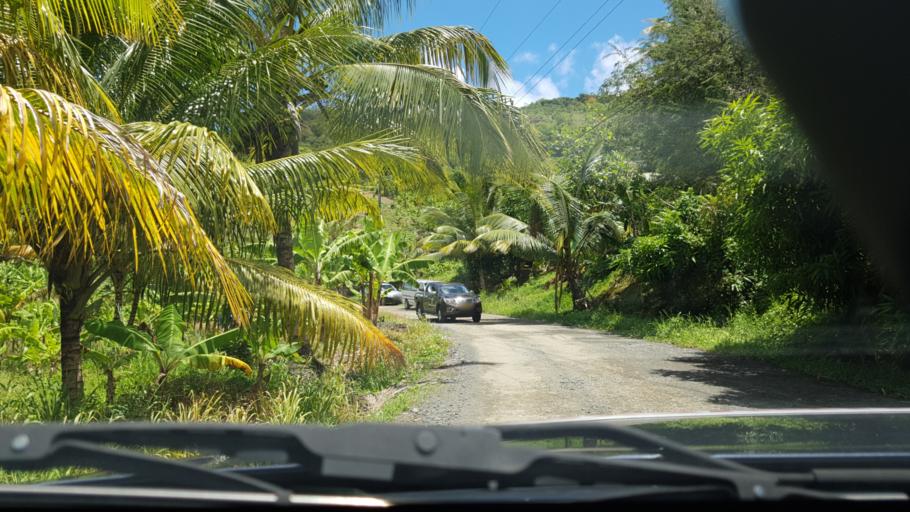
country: LC
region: Anse-la-Raye
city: Anse La Raye
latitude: 13.9468
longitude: -60.9895
